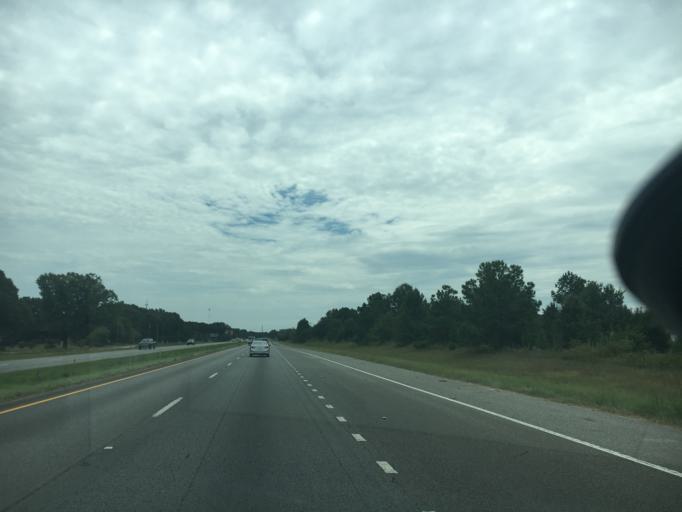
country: US
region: South Carolina
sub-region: Greenville County
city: Fountain Inn
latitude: 34.6608
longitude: -82.1718
